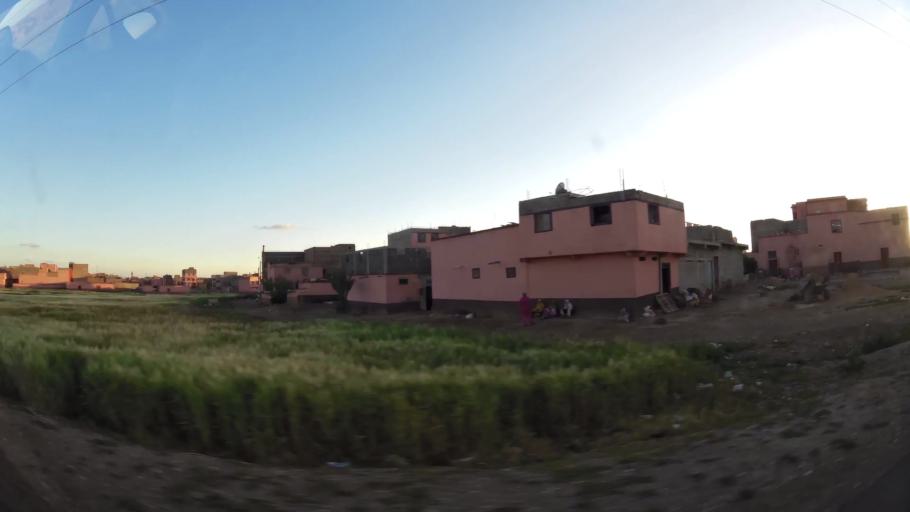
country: MA
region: Marrakech-Tensift-Al Haouz
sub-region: Kelaa-Des-Sraghna
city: Sidi Abdallah
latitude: 32.2402
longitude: -7.9310
